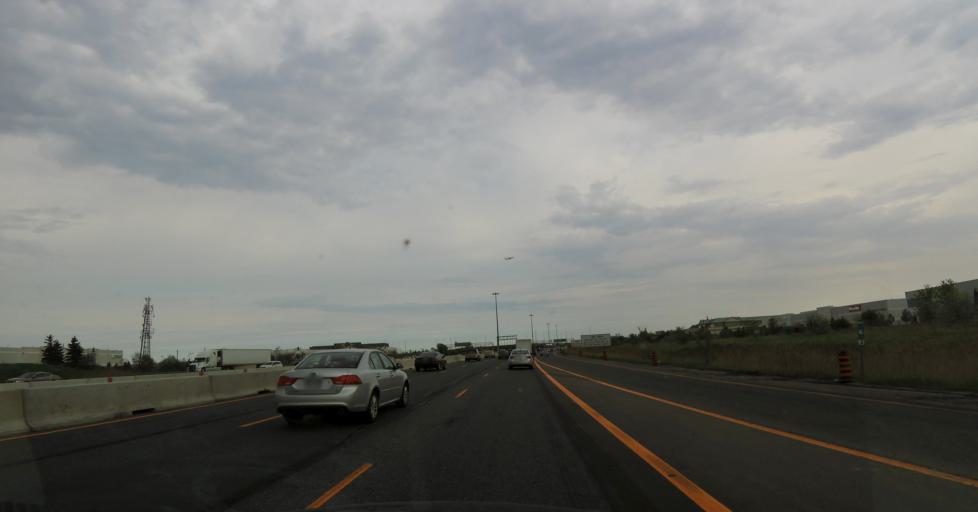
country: CA
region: Ontario
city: Brampton
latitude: 43.6822
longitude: -79.7085
